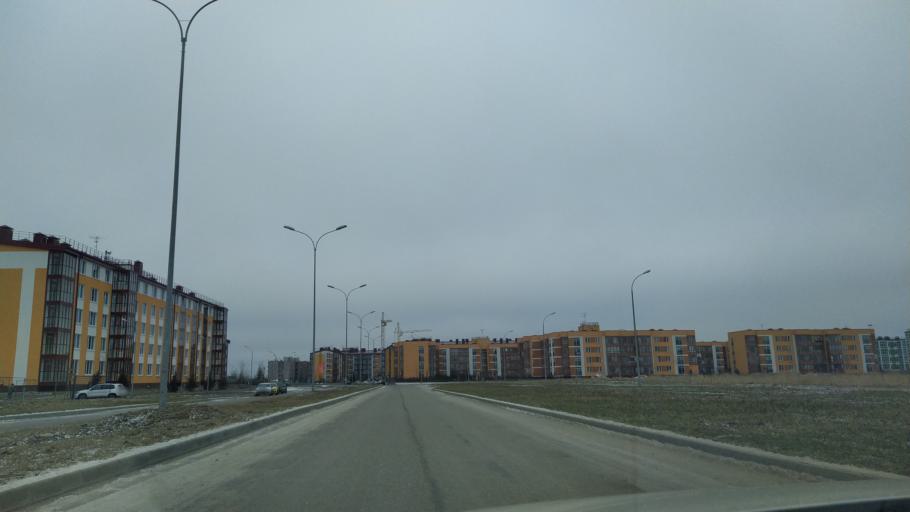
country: RU
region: St.-Petersburg
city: Aleksandrovskaya
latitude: 59.7536
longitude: 30.3628
